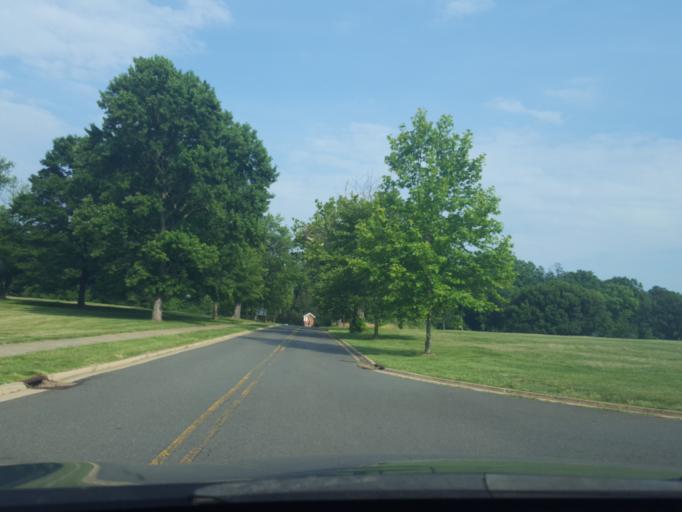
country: US
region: Maryland
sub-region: Prince George's County
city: Fort Washington
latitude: 38.7134
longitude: -77.0261
